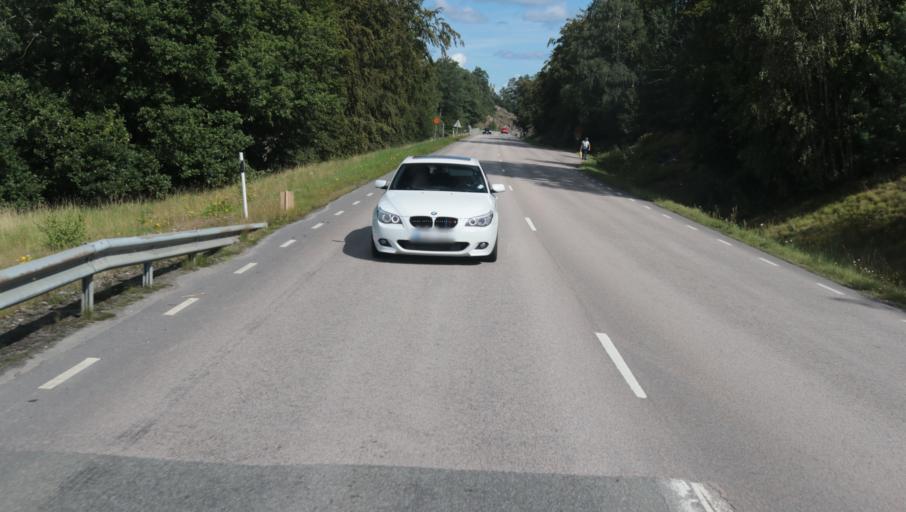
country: SE
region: Blekinge
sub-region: Karlshamns Kommun
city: Karlshamn
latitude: 56.1757
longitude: 14.8379
